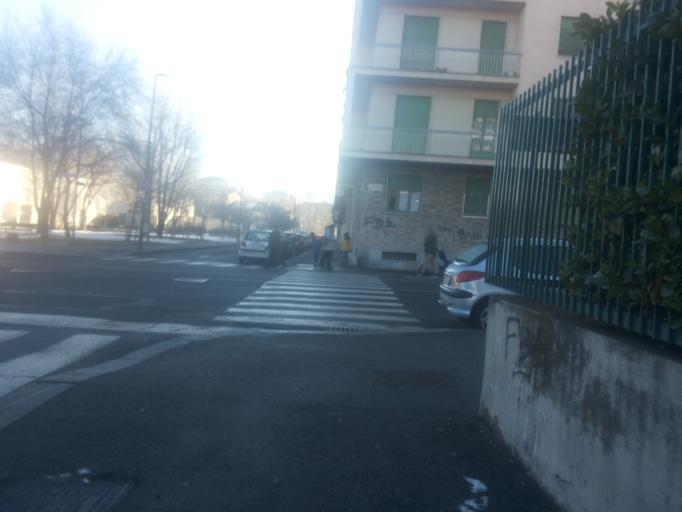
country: IT
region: Piedmont
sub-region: Provincia di Torino
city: Lesna
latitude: 45.0573
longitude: 7.6509
